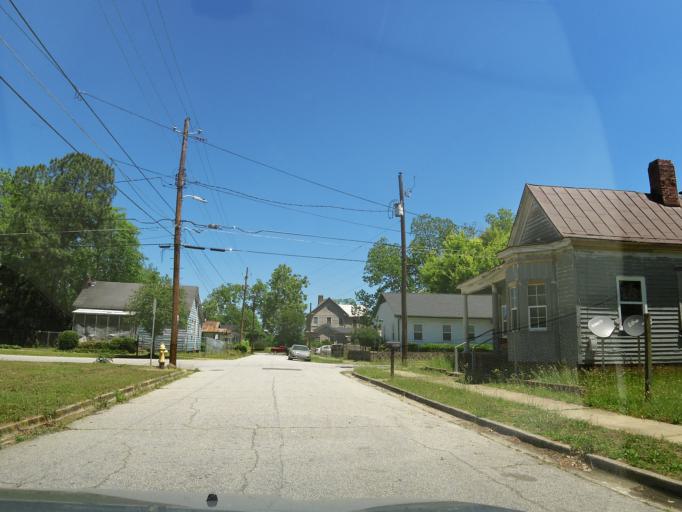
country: US
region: Georgia
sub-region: Richmond County
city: Augusta
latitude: 33.4671
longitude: -81.9747
